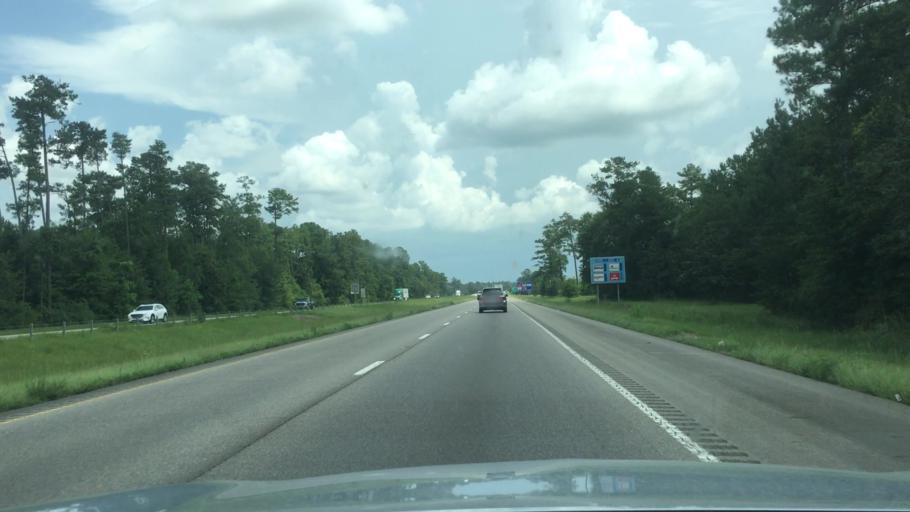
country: US
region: Mississippi
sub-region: Pearl River County
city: Picayune
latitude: 30.5063
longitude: -89.6672
